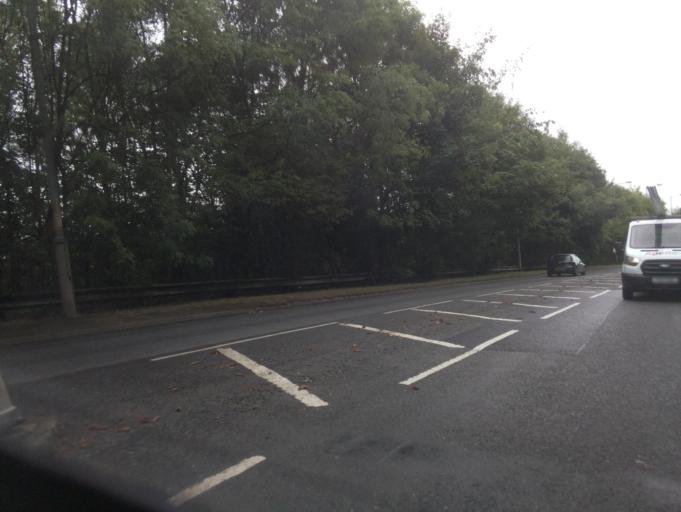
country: GB
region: England
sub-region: City and Borough of Wakefield
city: Crigglestone
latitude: 53.6486
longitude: -1.5406
